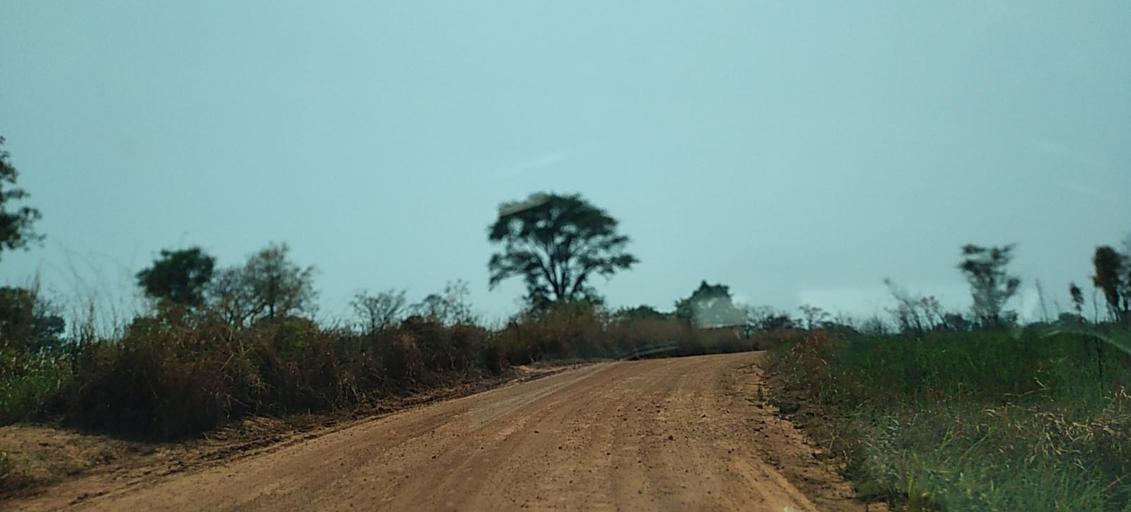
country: ZM
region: North-Western
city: Kansanshi
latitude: -12.0035
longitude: 26.5569
